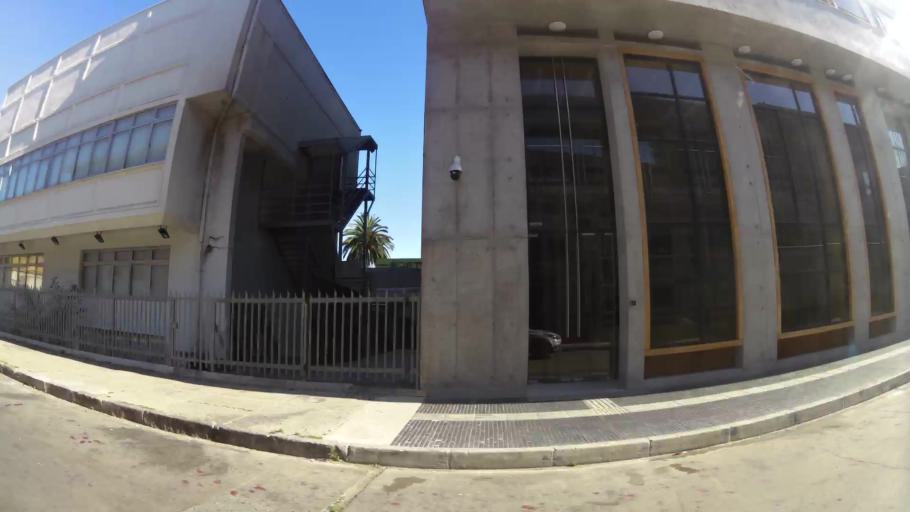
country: CL
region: Valparaiso
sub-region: Provincia de Valparaiso
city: Valparaiso
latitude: -33.0442
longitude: -71.6163
